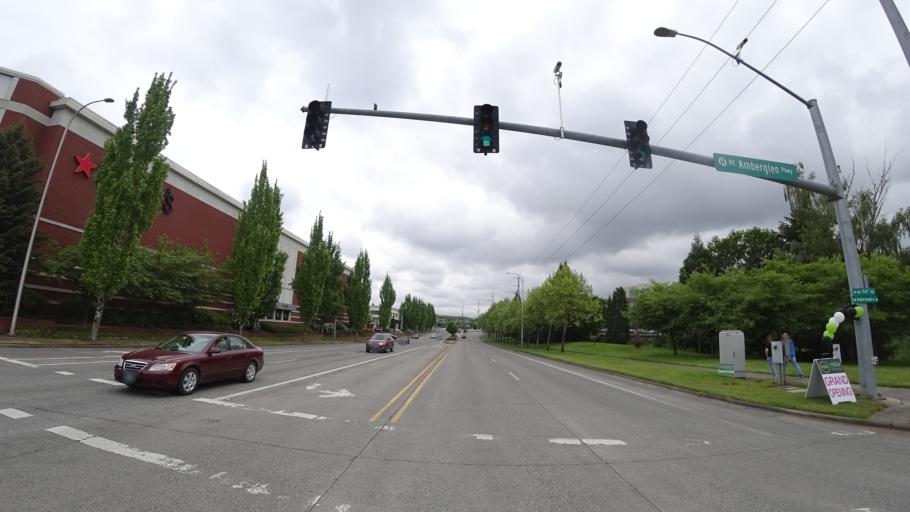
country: US
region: Oregon
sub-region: Washington County
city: Rockcreek
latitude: 45.5357
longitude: -122.8809
